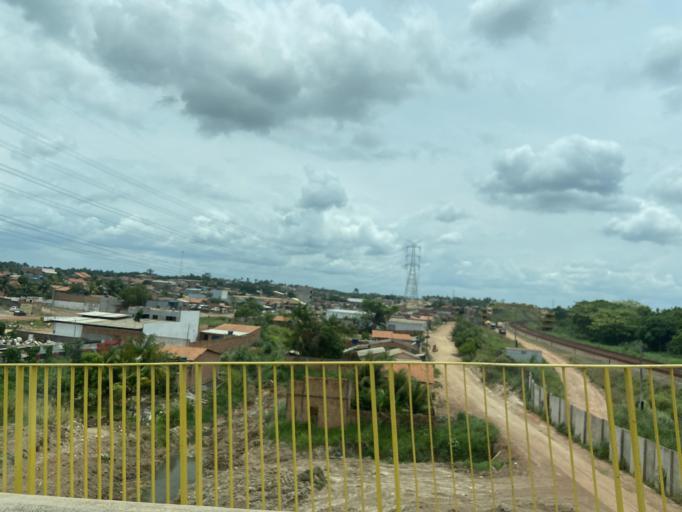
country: BR
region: Para
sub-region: Maraba
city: Maraba
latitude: -5.3492
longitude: -49.0745
